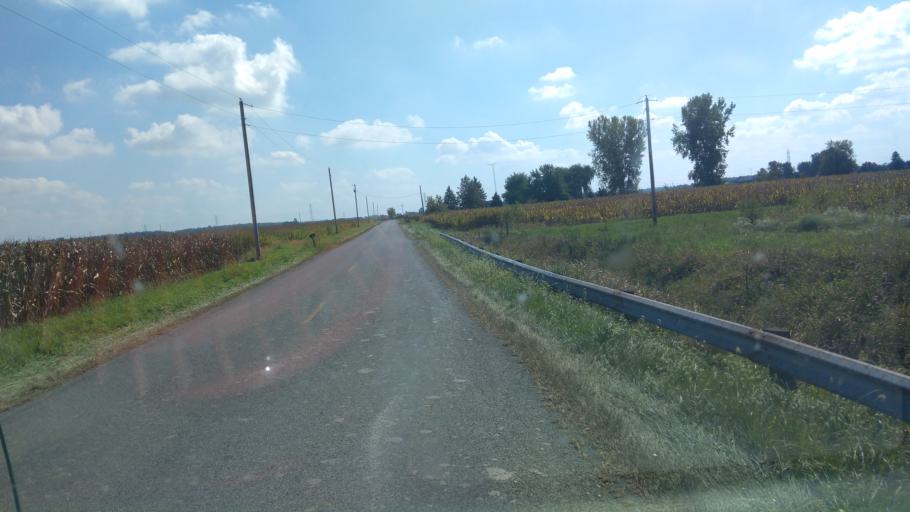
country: US
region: Ohio
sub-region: Hardin County
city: Ada
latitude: 40.6789
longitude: -83.8421
